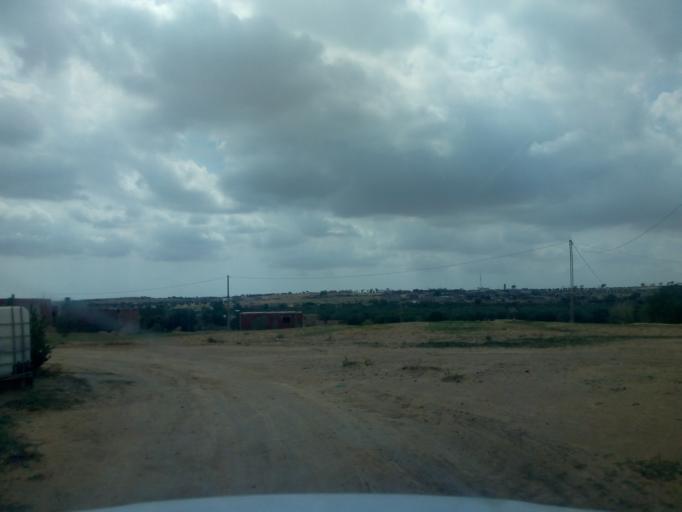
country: TN
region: Safaqis
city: Sfax
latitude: 34.7417
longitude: 10.4929
